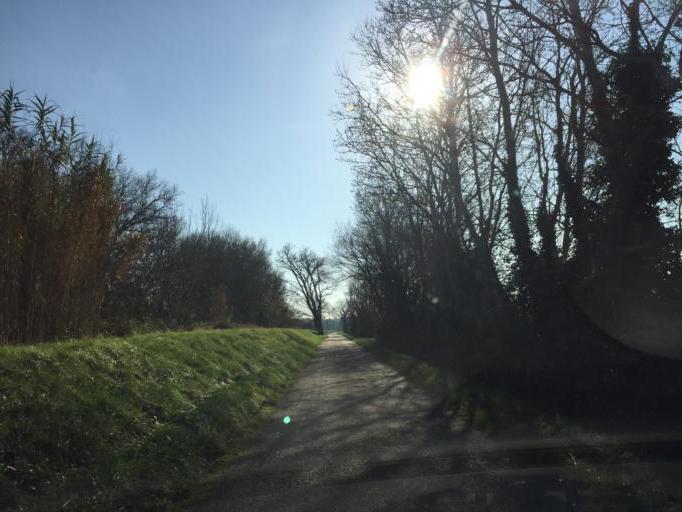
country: FR
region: Provence-Alpes-Cote d'Azur
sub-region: Departement du Vaucluse
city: Bedarrides
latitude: 44.0499
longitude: 4.9283
